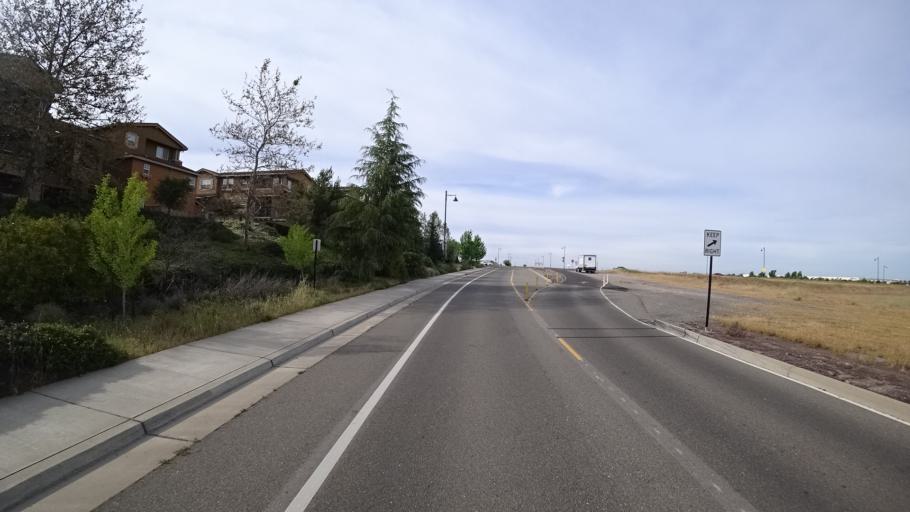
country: US
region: California
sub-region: Placer County
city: Lincoln
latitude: 38.8320
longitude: -121.2926
